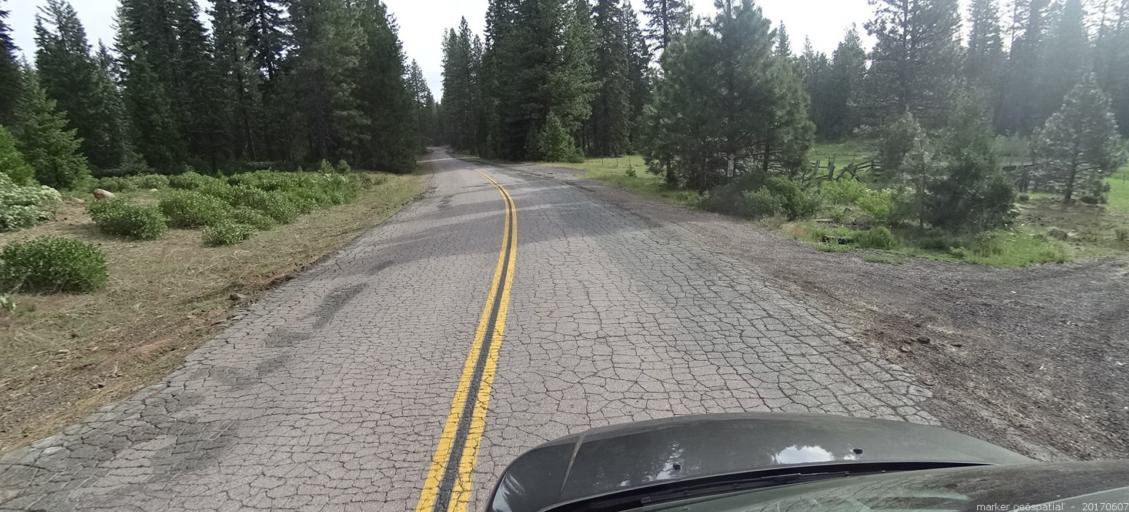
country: US
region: California
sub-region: Shasta County
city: Burney
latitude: 41.1799
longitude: -121.7087
